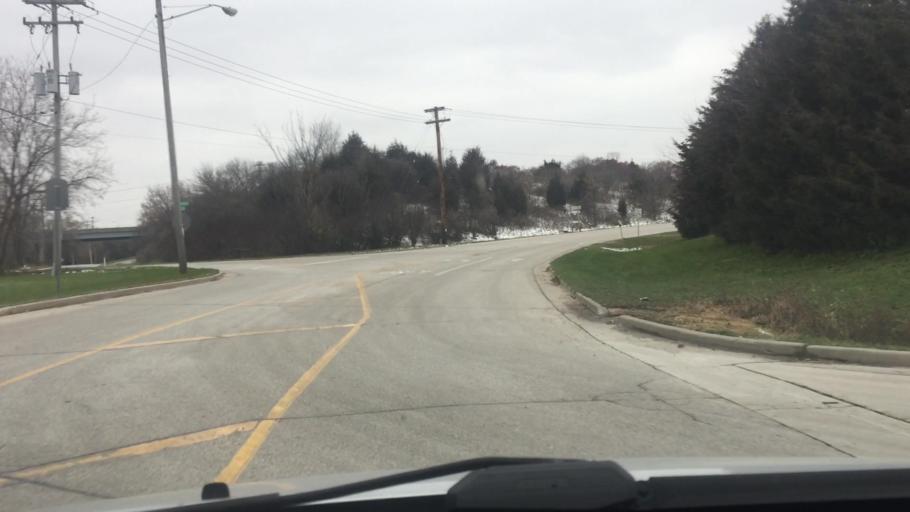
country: US
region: Wisconsin
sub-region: Waukesha County
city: Hartland
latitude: 43.1006
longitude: -88.3592
